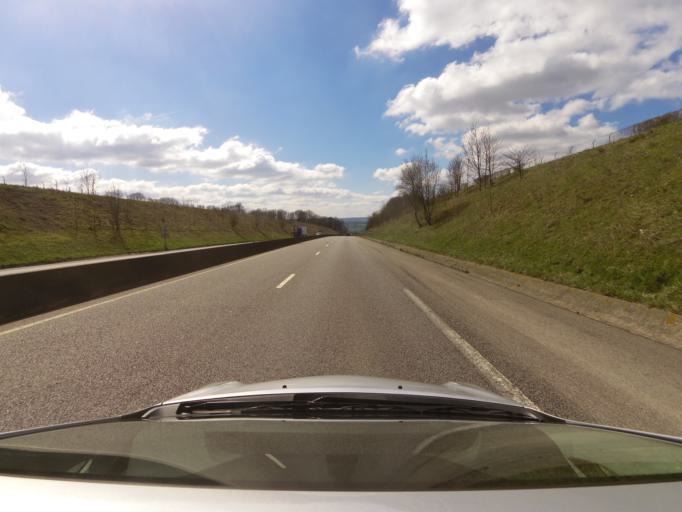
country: FR
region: Haute-Normandie
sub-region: Departement de la Seine-Maritime
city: Neufchatel-en-Bray
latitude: 49.7388
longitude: 1.4710
